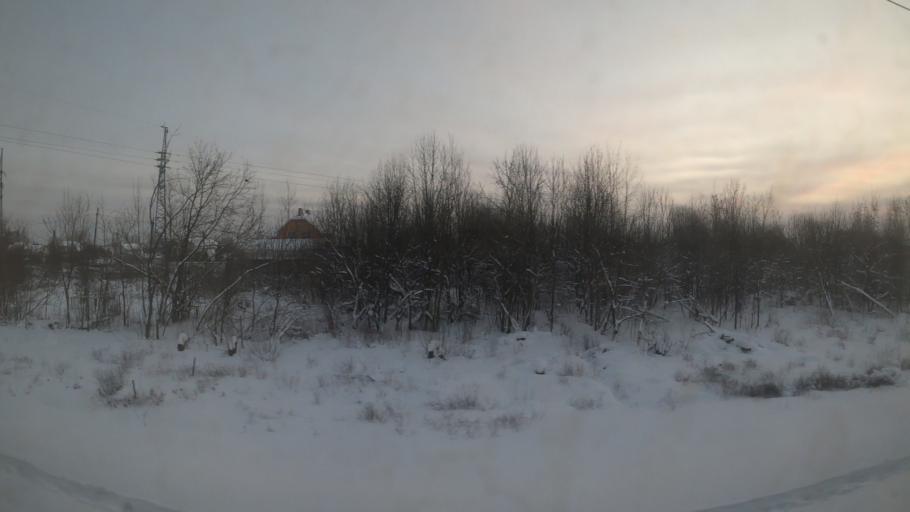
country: RU
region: Moskovskaya
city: Lobnya
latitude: 56.0057
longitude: 37.4886
